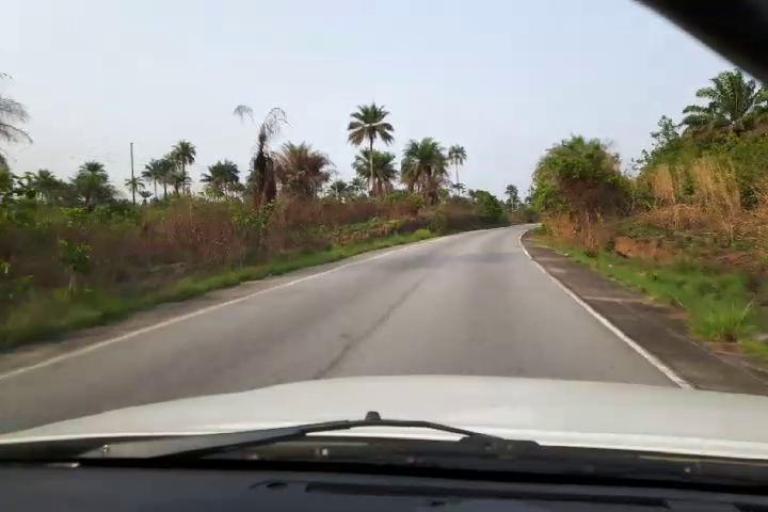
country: SL
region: Eastern Province
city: Blama
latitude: 7.9407
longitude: -11.5038
